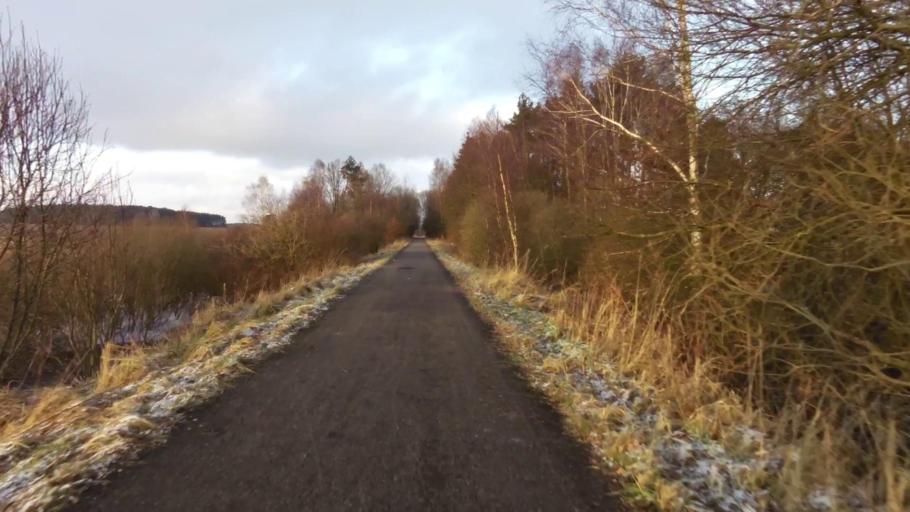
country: PL
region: West Pomeranian Voivodeship
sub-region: Powiat drawski
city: Zlocieniec
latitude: 53.6048
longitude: 16.0469
